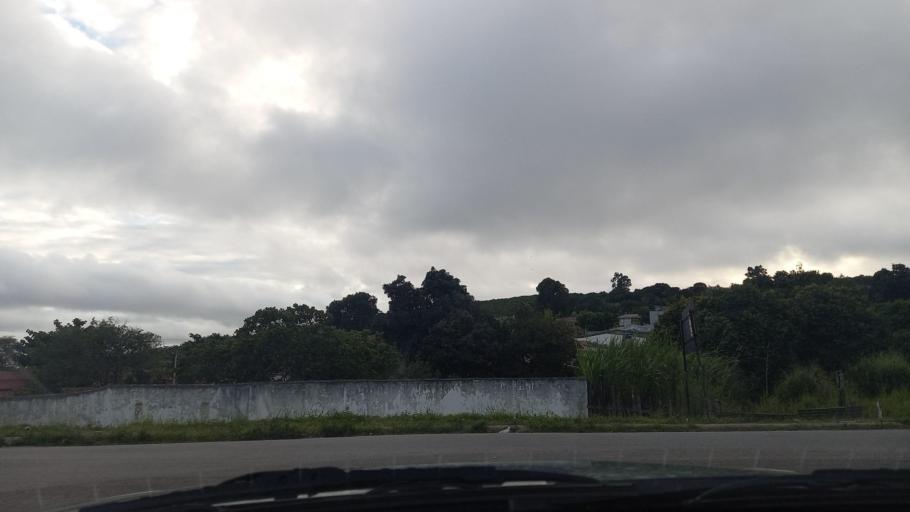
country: BR
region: Pernambuco
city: Garanhuns
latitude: -8.8793
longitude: -36.5069
